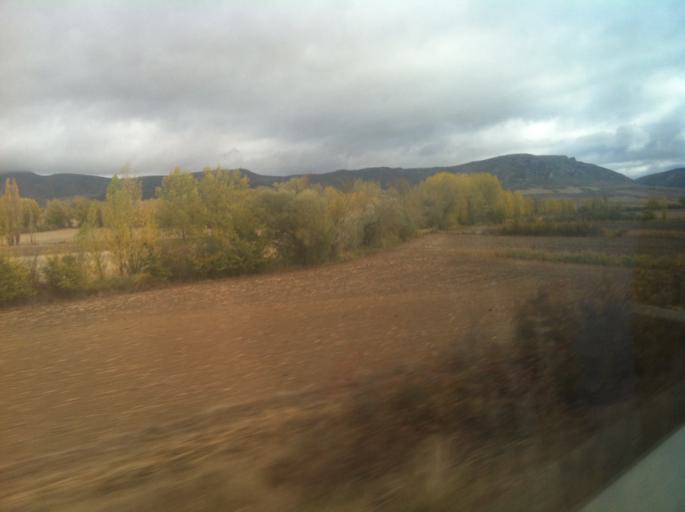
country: ES
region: Castille and Leon
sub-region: Provincia de Burgos
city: Villanueva de Teba
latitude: 42.6248
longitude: -3.1779
